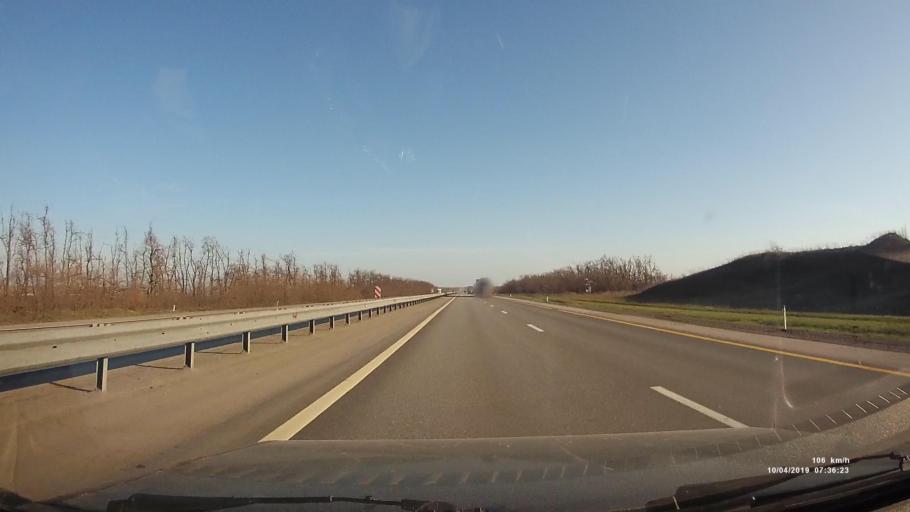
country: RU
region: Rostov
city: Likhoy
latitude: 48.0564
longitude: 40.2595
